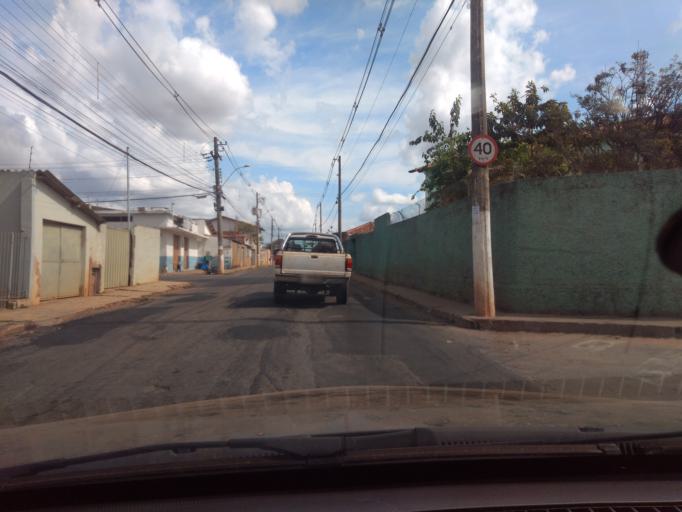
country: BR
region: Minas Gerais
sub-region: Tres Coracoes
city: Tres Coracoes
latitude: -21.7045
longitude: -45.2494
